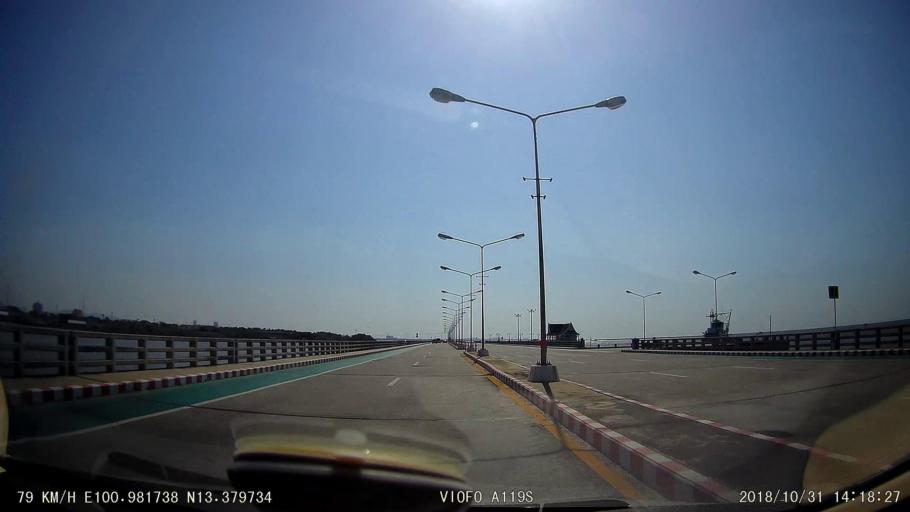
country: TH
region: Chon Buri
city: Chon Buri
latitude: 13.3797
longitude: 100.9817
